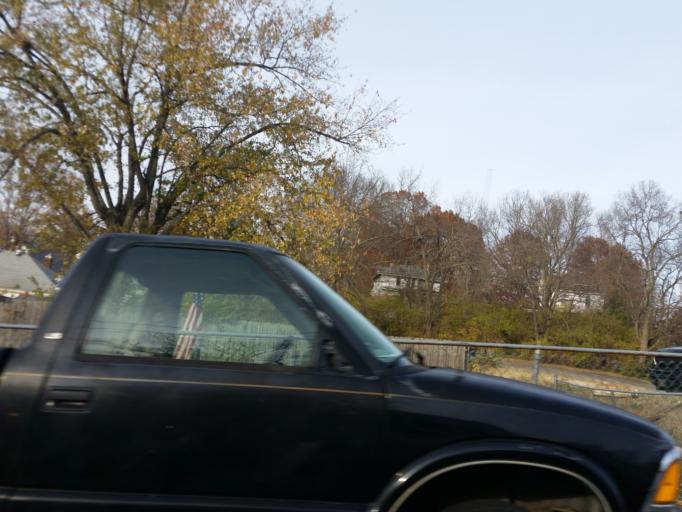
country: US
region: Kentucky
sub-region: Harrison County
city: Cynthiana
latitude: 38.3870
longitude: -84.2862
